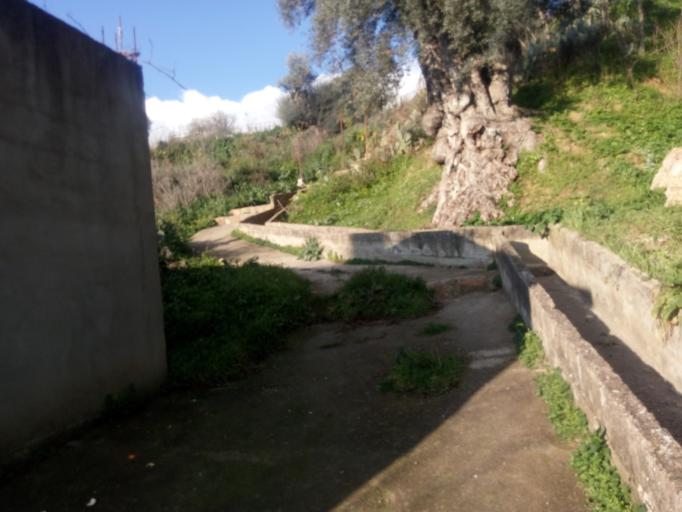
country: DZ
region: Tizi Ouzou
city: Chemini
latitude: 36.6028
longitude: 4.6369
